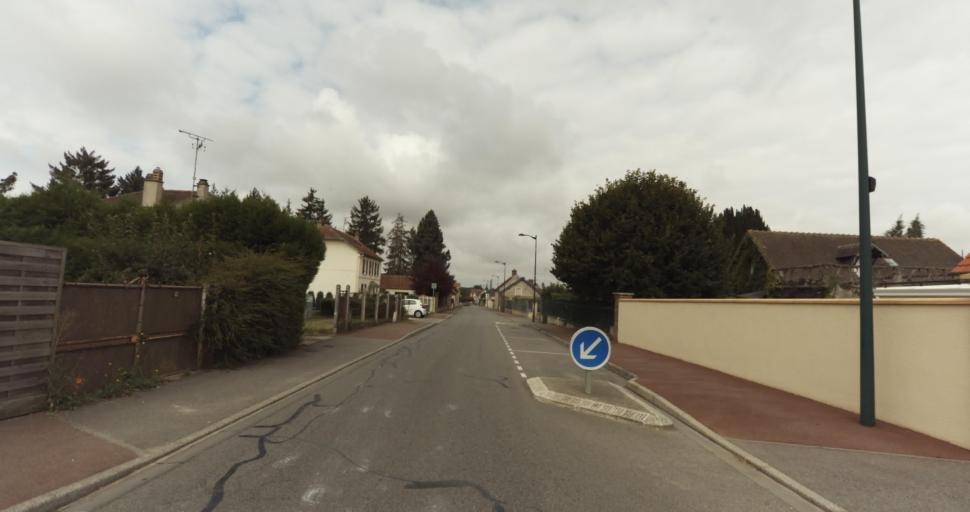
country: FR
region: Haute-Normandie
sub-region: Departement de l'Eure
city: La Couture-Boussey
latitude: 48.8970
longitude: 1.4116
